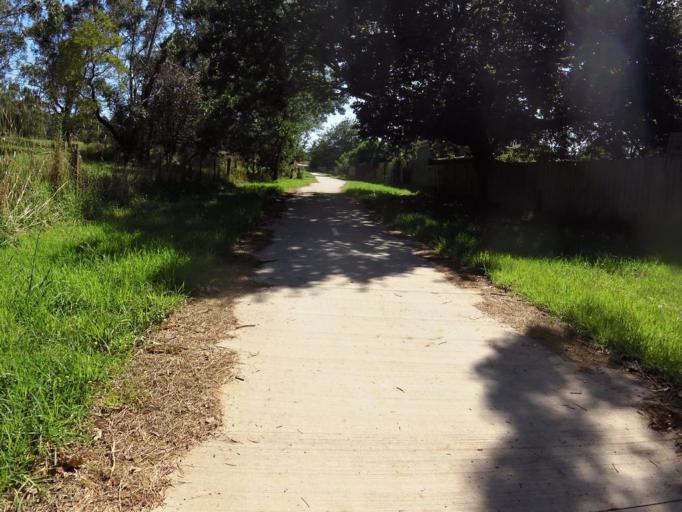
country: AU
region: Victoria
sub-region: Yarra Ranges
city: Kilsyth
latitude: -37.7775
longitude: 145.3317
